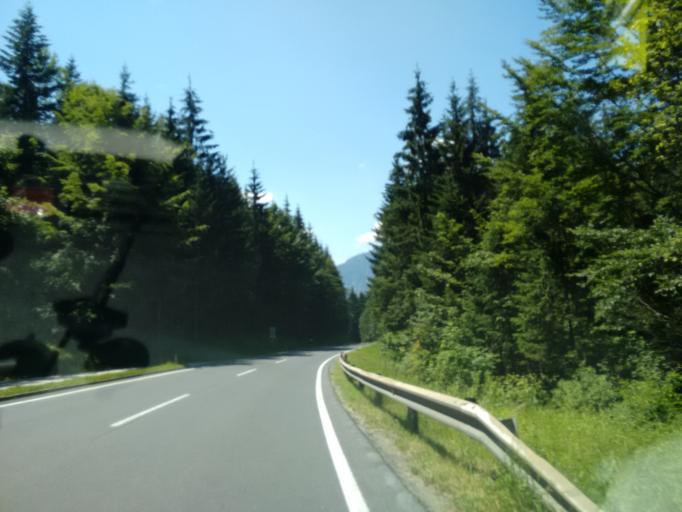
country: AT
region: Upper Austria
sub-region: Politischer Bezirk Gmunden
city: Bad Goisern
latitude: 47.6240
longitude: 13.6834
